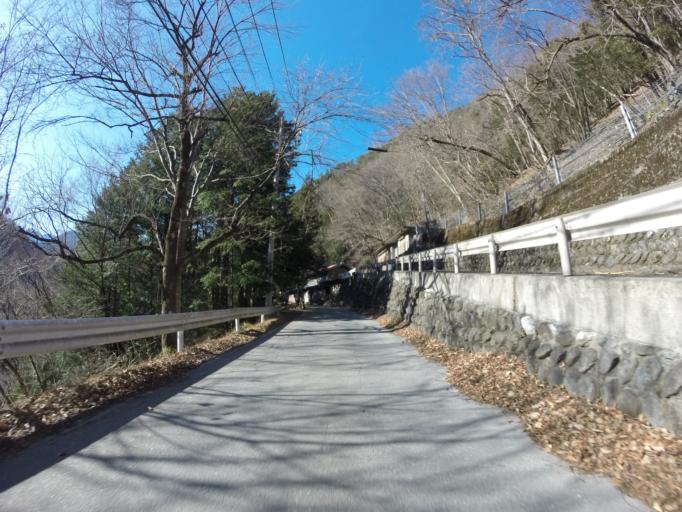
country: JP
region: Yamanashi
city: Ryuo
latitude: 35.4145
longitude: 138.3464
